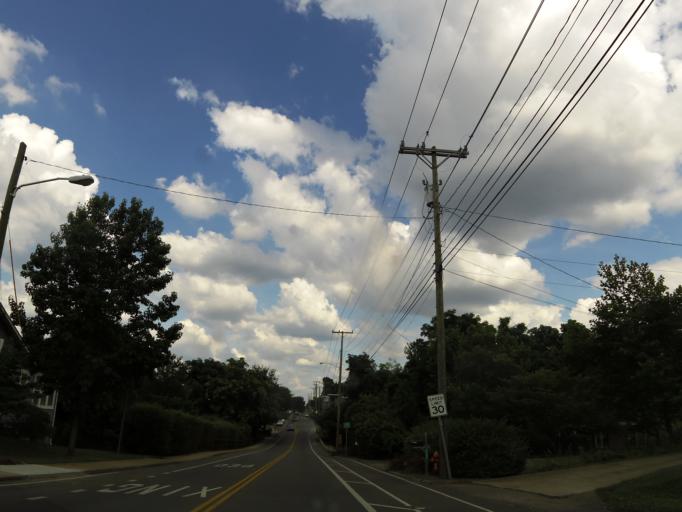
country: US
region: Tennessee
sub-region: Davidson County
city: Nashville
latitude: 36.1826
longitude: -86.7379
